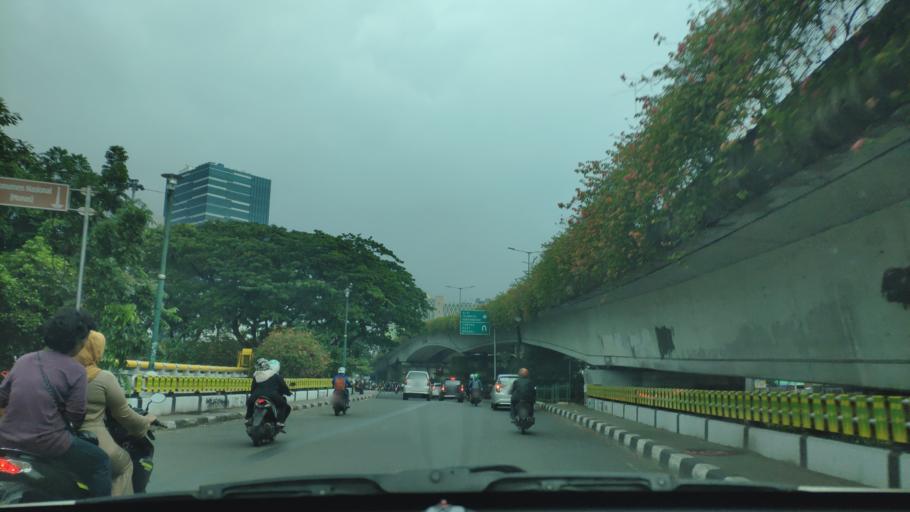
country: ID
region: Jakarta Raya
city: Jakarta
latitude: -6.1812
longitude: 106.8135
